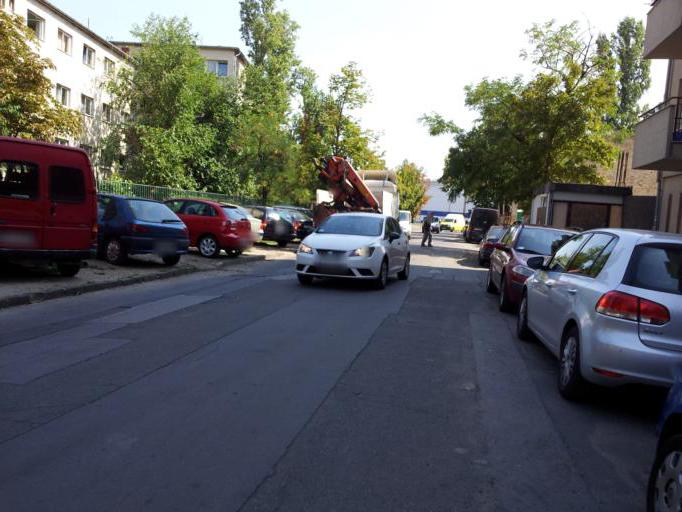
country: HU
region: Budapest
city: Budapest XIV. keruelet
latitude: 47.5042
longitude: 19.1146
